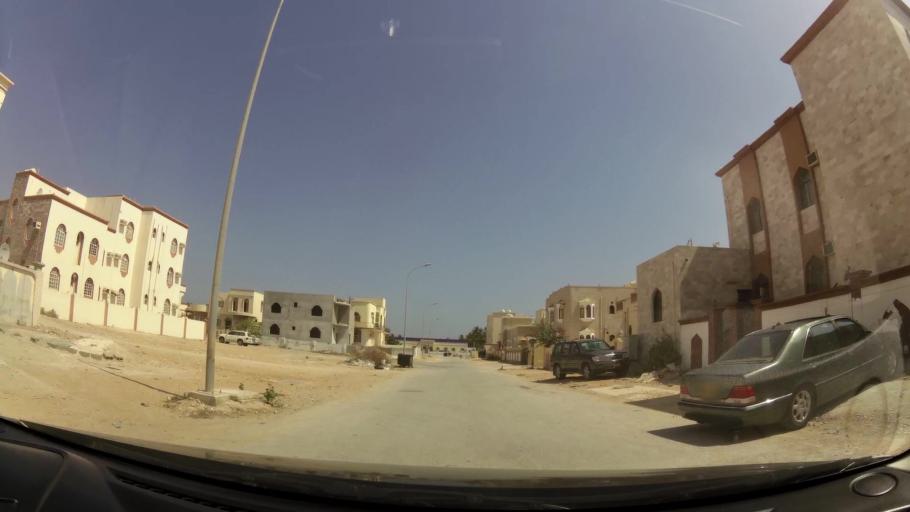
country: OM
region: Zufar
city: Salalah
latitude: 17.0404
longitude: 54.1549
